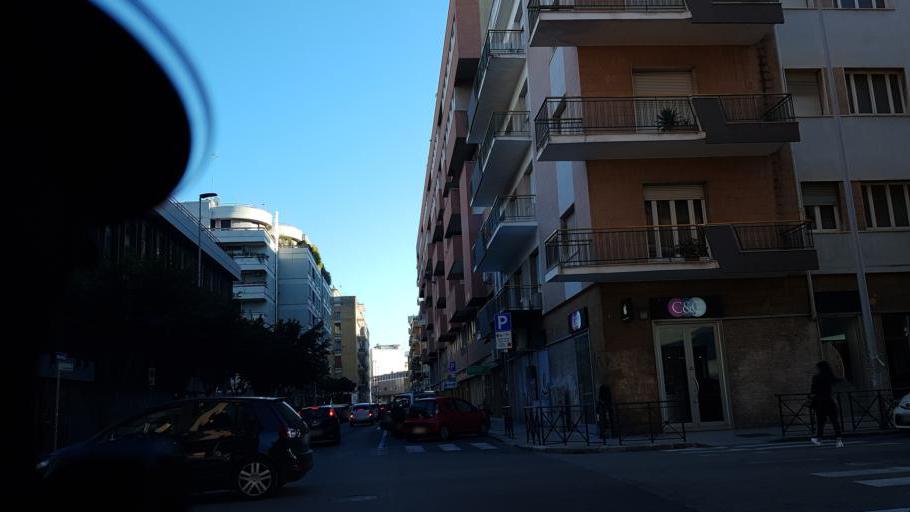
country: IT
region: Apulia
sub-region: Provincia di Lecce
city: Lecce
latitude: 40.3542
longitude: 18.1820
